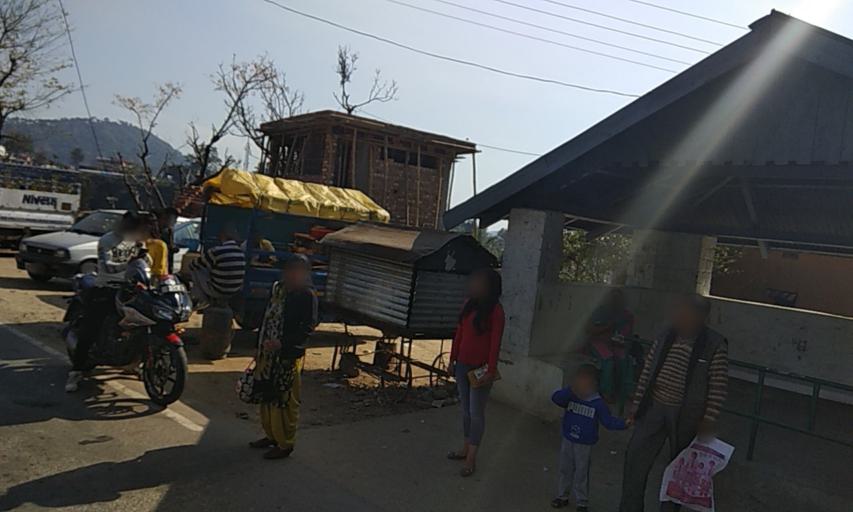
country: IN
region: Himachal Pradesh
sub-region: Kangra
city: Dharmsala
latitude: 32.1508
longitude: 76.4174
